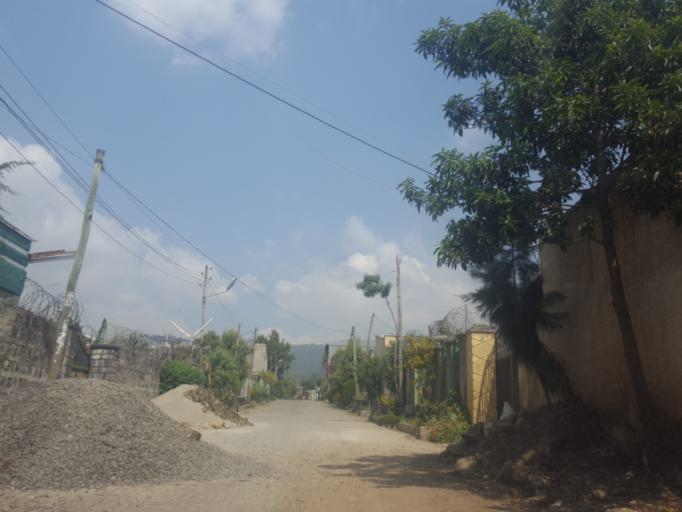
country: ET
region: Adis Abeba
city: Addis Ababa
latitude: 9.0626
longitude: 38.7224
